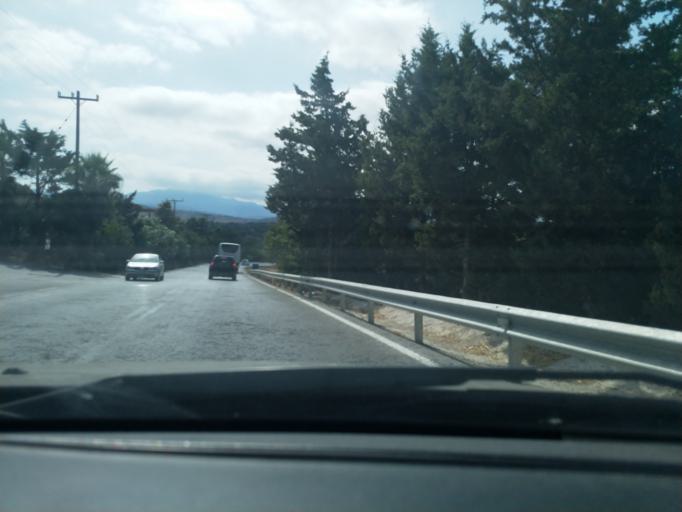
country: GR
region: Crete
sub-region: Nomos Rethymnis
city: Atsipopoulon
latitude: 35.2991
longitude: 24.4628
